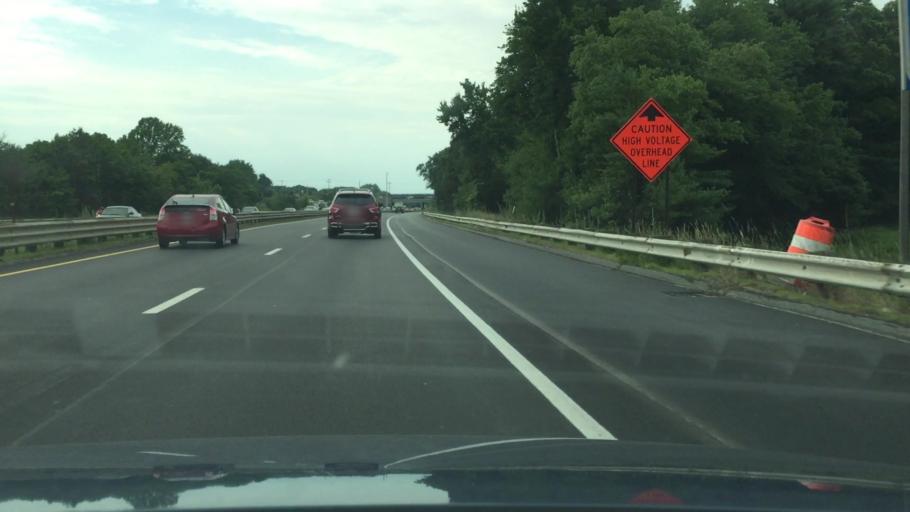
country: US
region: Massachusetts
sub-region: Plymouth County
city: Kingston
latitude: 41.9841
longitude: -70.7165
